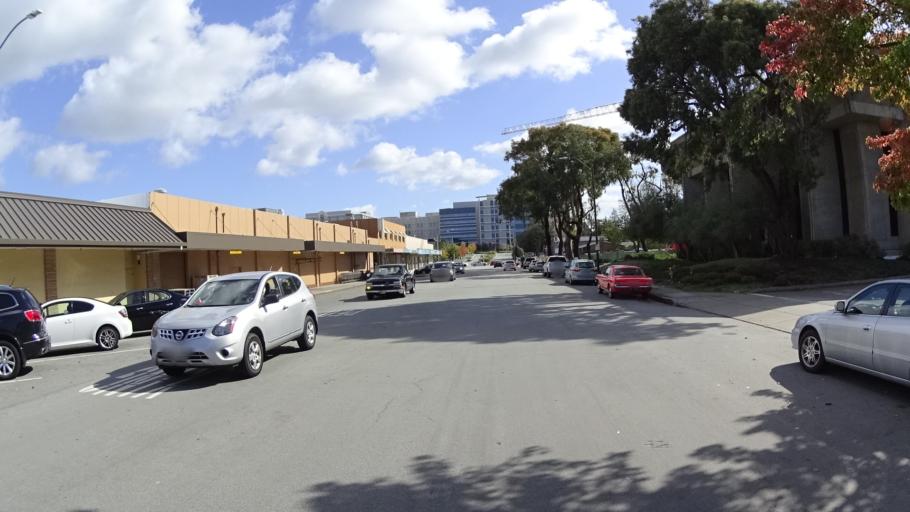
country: US
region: California
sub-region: San Mateo County
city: Millbrae
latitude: 37.5945
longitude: -122.3857
